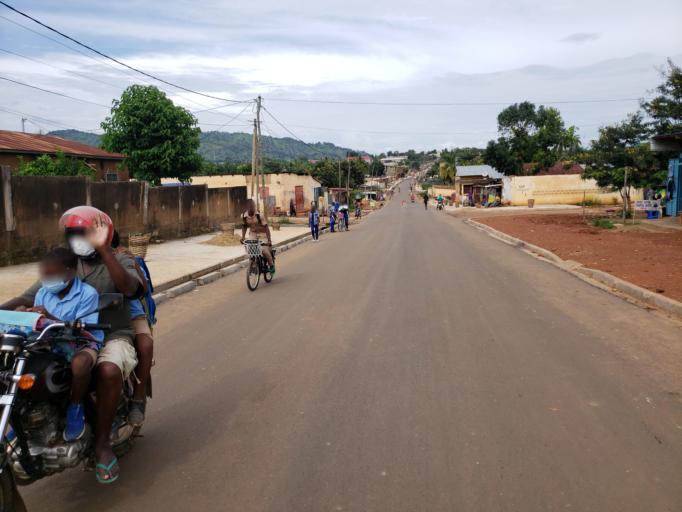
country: TG
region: Kara
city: Kara
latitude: 9.5560
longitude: 1.1960
